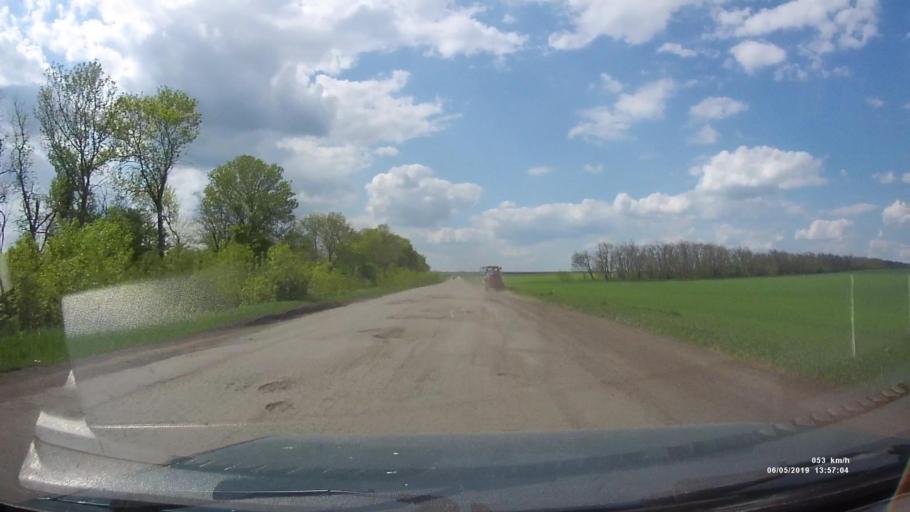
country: RU
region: Rostov
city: Shakhty
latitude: 47.6830
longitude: 40.4241
